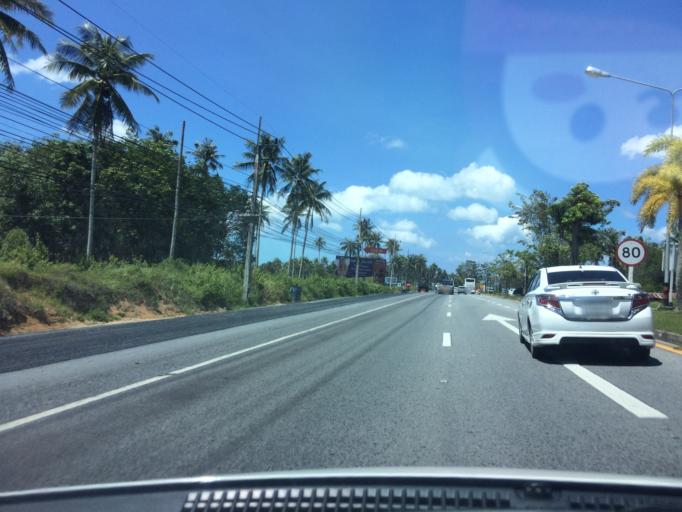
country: TH
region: Phuket
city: Thalang
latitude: 8.1655
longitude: 98.3033
